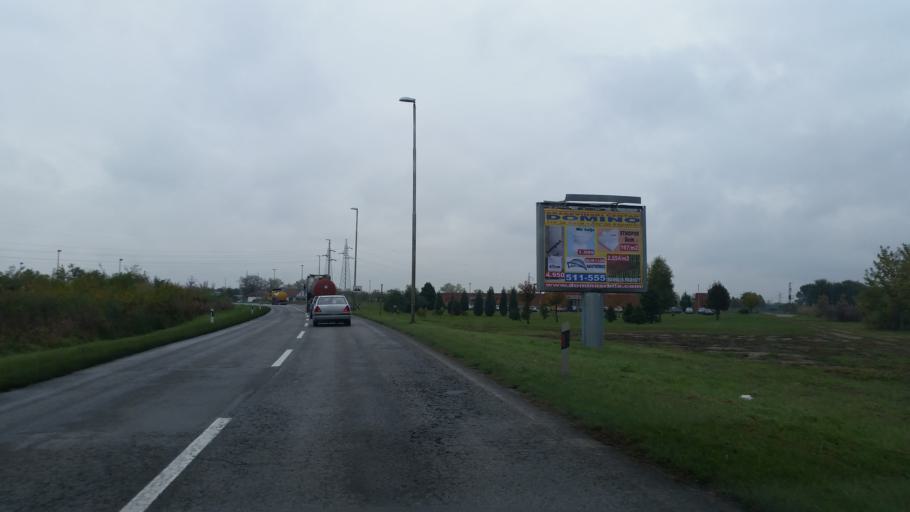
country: RS
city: Ecka
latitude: 45.3590
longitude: 20.4218
